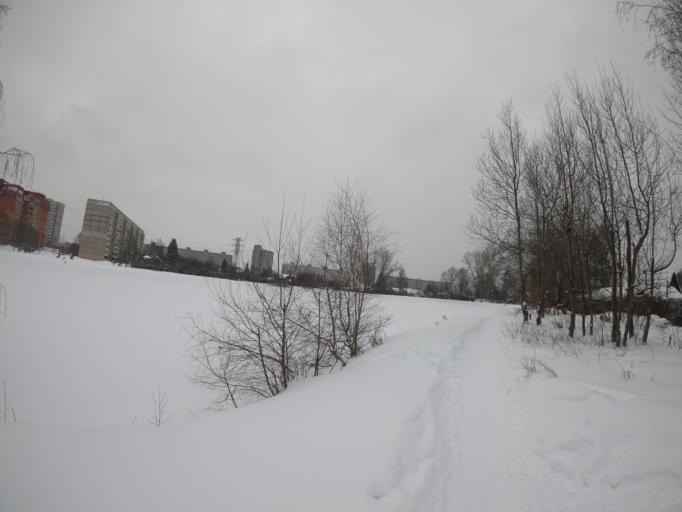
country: RU
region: Moskovskaya
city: Vostryakovo
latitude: 55.4161
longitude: 37.8271
